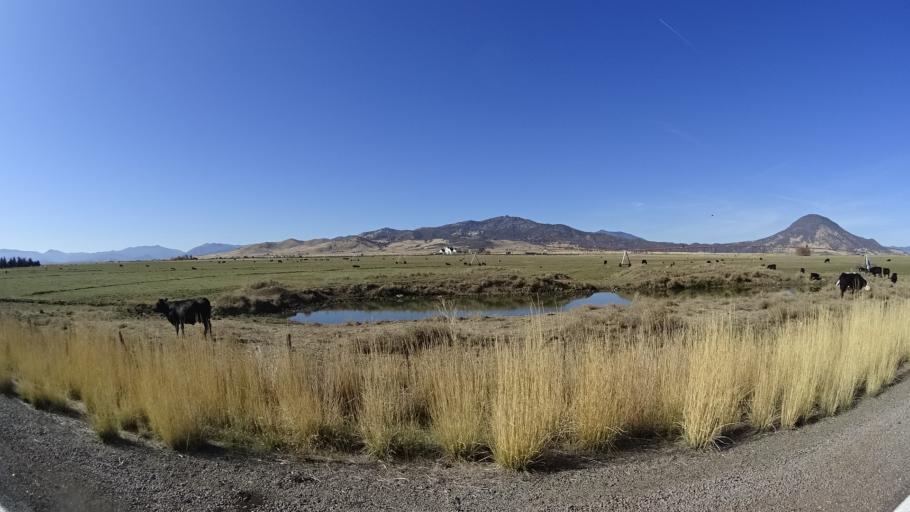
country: US
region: California
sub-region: Siskiyou County
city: Montague
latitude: 41.7895
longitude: -122.4715
